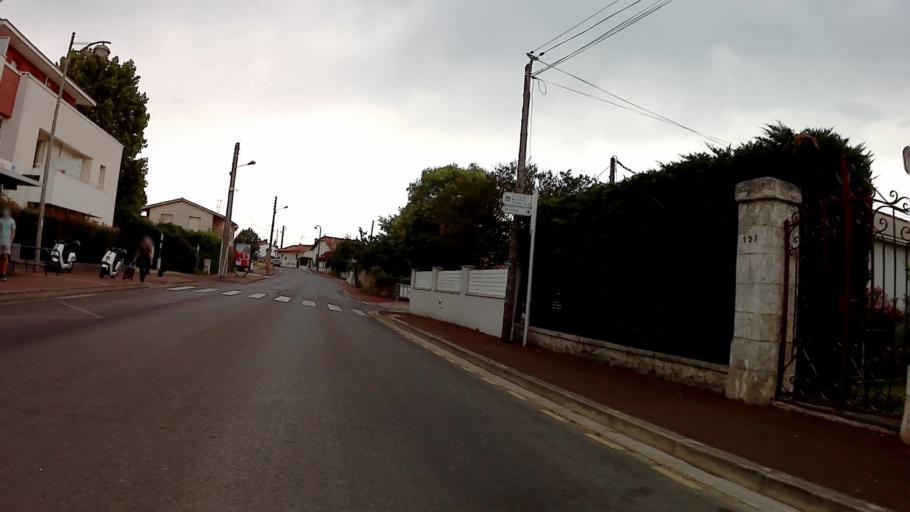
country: FR
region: Aquitaine
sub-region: Departement de la Gironde
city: Le Bouscat
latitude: 44.8657
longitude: -0.5906
